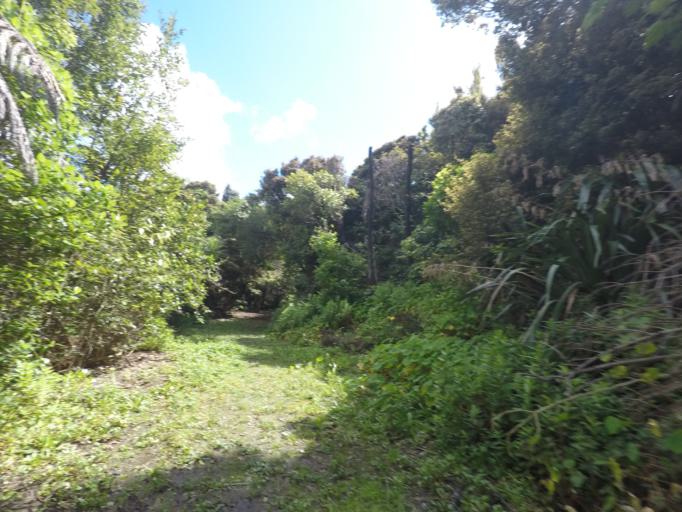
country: NZ
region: Auckland
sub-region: Auckland
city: Rosebank
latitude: -36.8805
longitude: 174.6691
